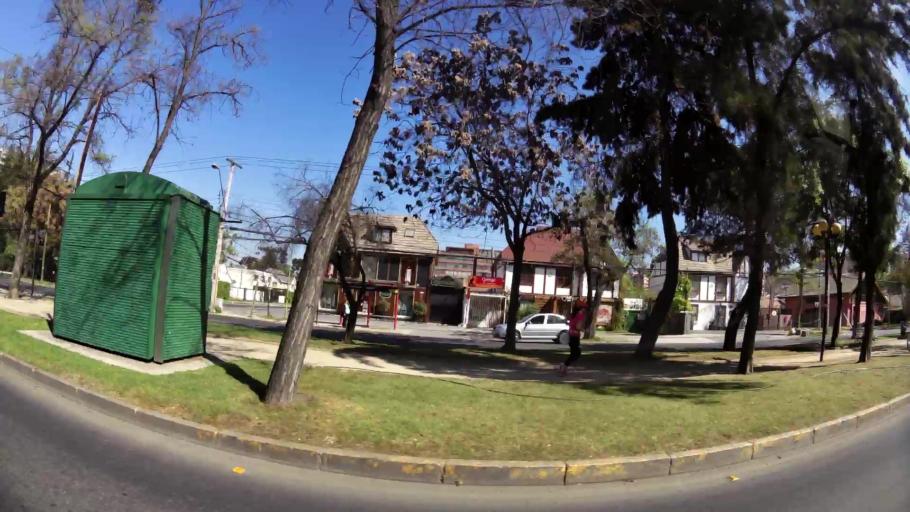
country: CL
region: Santiago Metropolitan
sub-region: Provincia de Santiago
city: Villa Presidente Frei, Nunoa, Santiago, Chile
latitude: -33.4205
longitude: -70.5643
